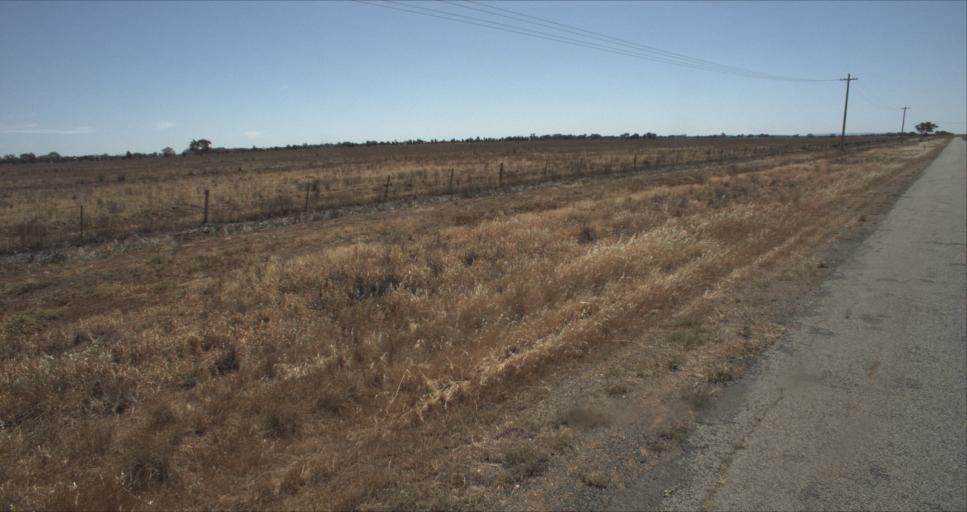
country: AU
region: New South Wales
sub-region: Leeton
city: Leeton
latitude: -34.5074
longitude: 146.3446
